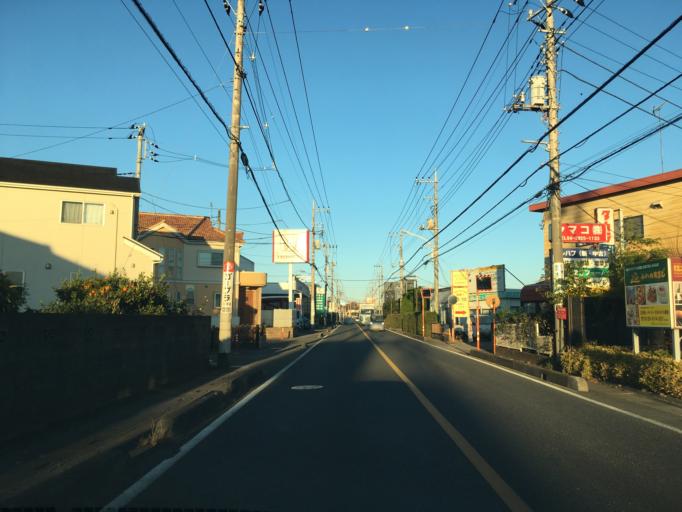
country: JP
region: Saitama
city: Tokorozawa
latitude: 35.8122
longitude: 139.4277
